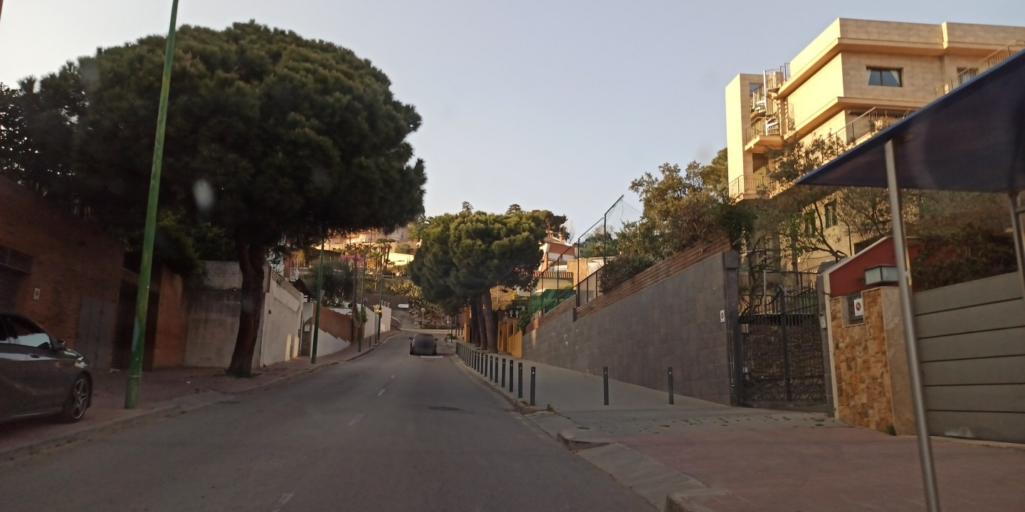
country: ES
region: Catalonia
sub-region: Provincia de Barcelona
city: Sant Just Desvern
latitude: 41.3869
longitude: 2.0850
